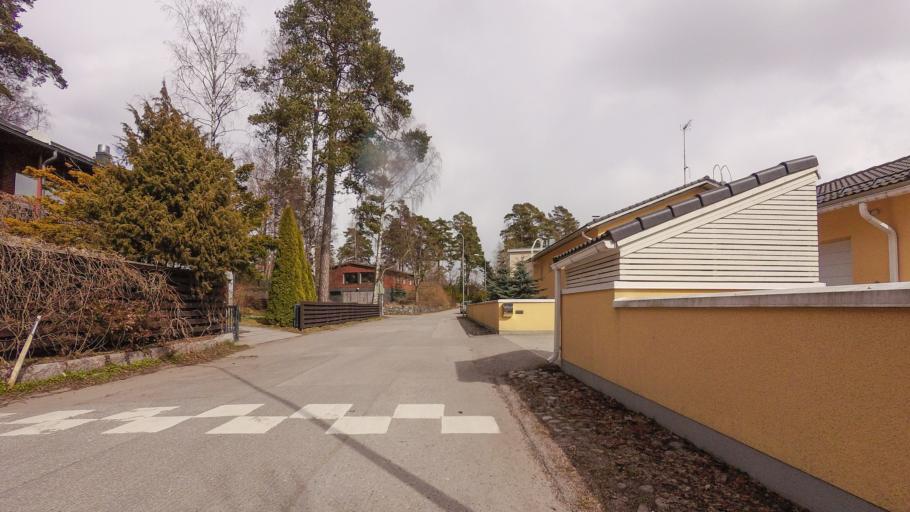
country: FI
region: Uusimaa
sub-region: Helsinki
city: Vantaa
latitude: 60.2016
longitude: 25.0933
